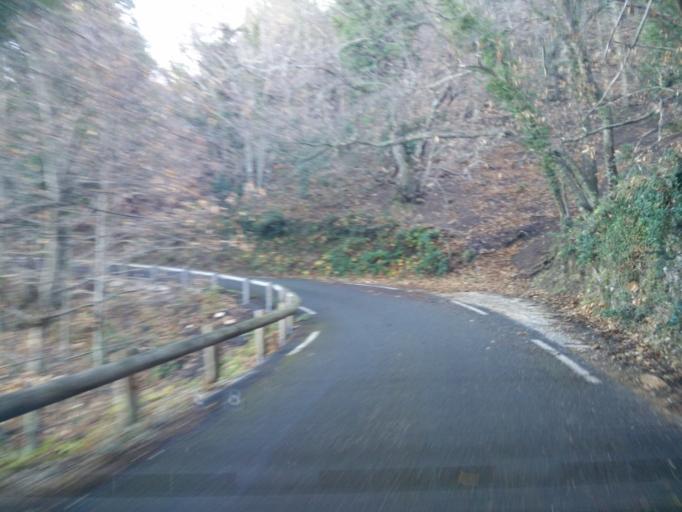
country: FR
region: Provence-Alpes-Cote d'Azur
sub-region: Departement du Var
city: Collobrieres
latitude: 43.2354
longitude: 6.3881
